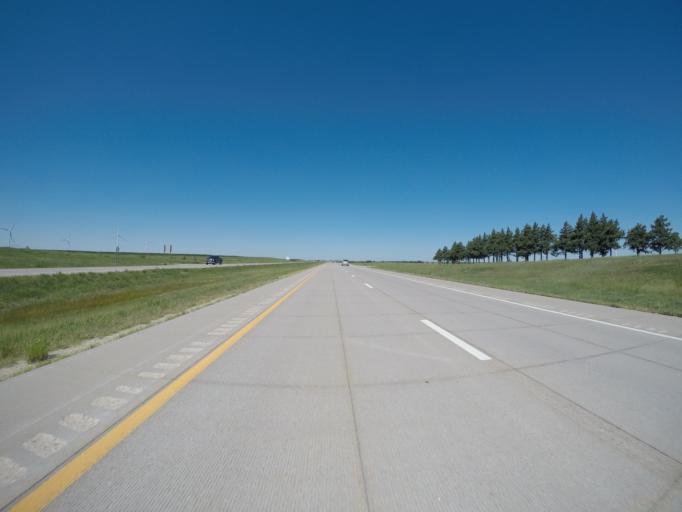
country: US
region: Kansas
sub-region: Ellsworth County
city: Ellsworth
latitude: 38.8494
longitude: -98.2825
